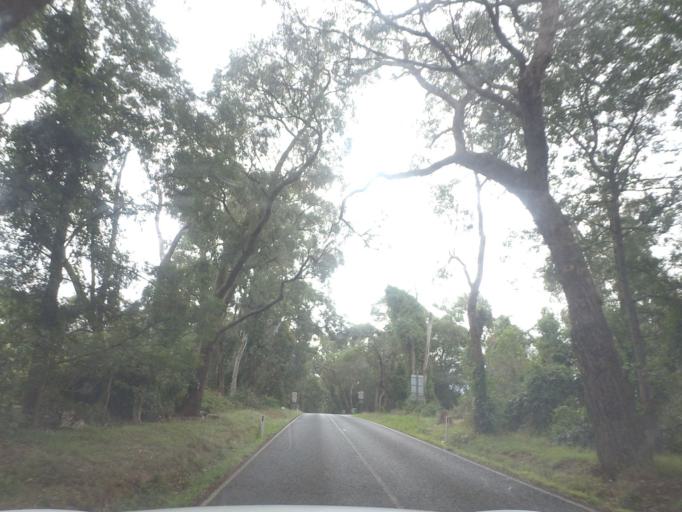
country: AU
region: Victoria
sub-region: Maroondah
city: Kilsyth South
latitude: -37.8305
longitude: 145.3264
